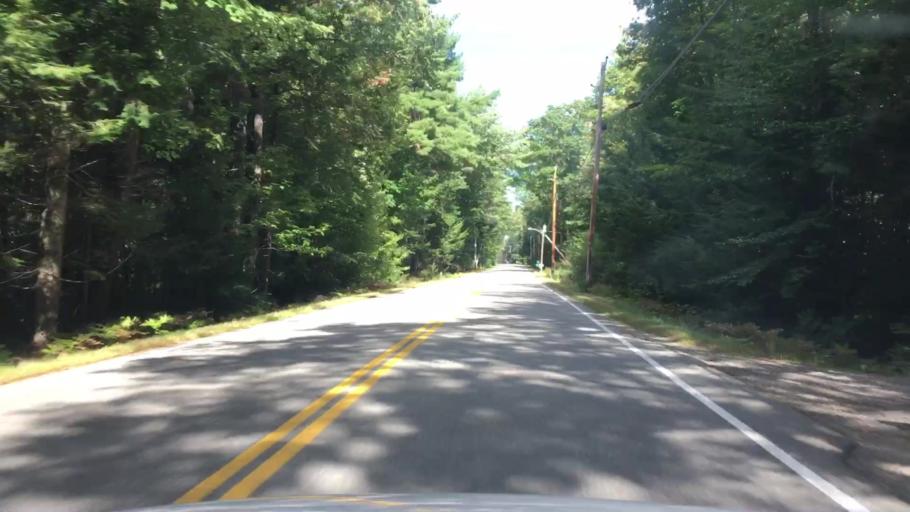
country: US
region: Maine
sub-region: Cumberland County
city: Westbrook
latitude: 43.6359
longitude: -70.4033
